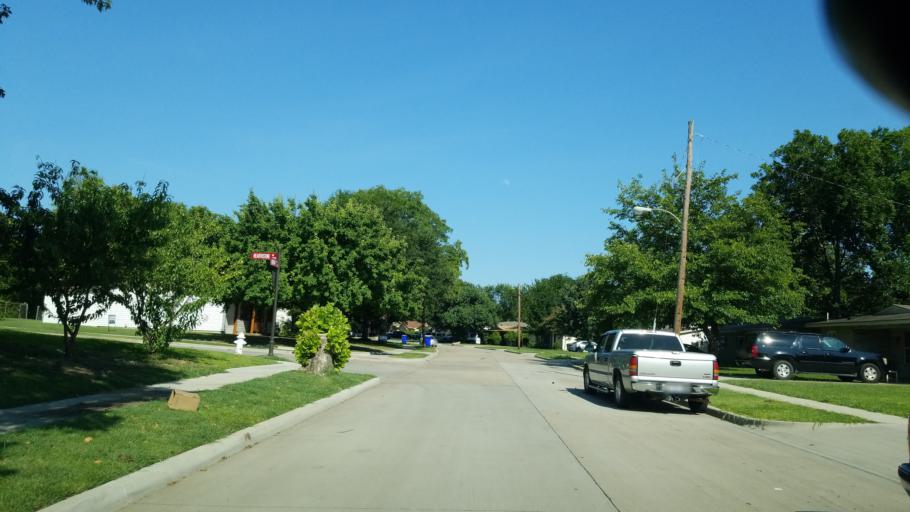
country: US
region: Texas
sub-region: Dallas County
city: Farmers Branch
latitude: 32.9329
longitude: -96.8948
